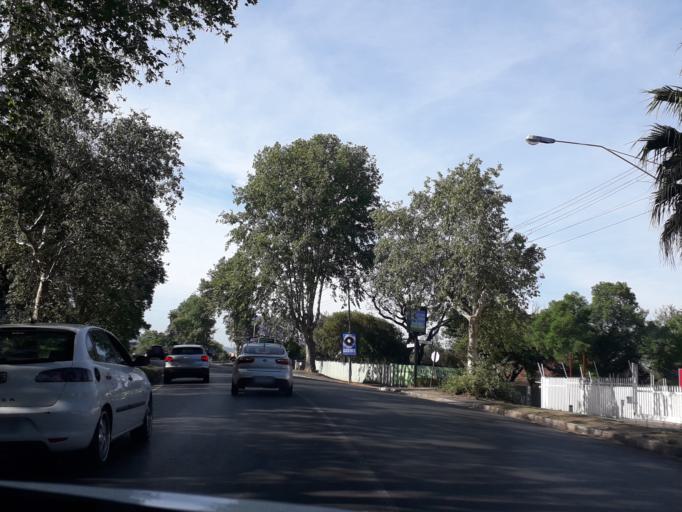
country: ZA
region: Gauteng
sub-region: City of Johannesburg Metropolitan Municipality
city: Johannesburg
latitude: -26.1377
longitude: 28.0344
